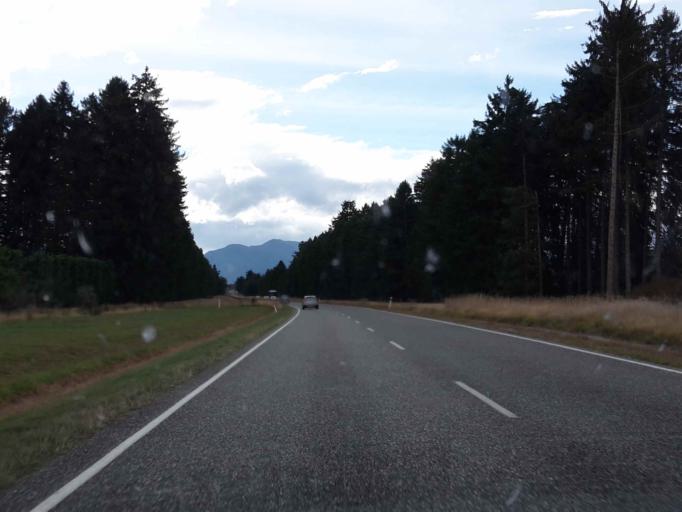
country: NZ
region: Otago
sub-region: Queenstown-Lakes District
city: Wanaka
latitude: -44.7305
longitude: 169.1367
